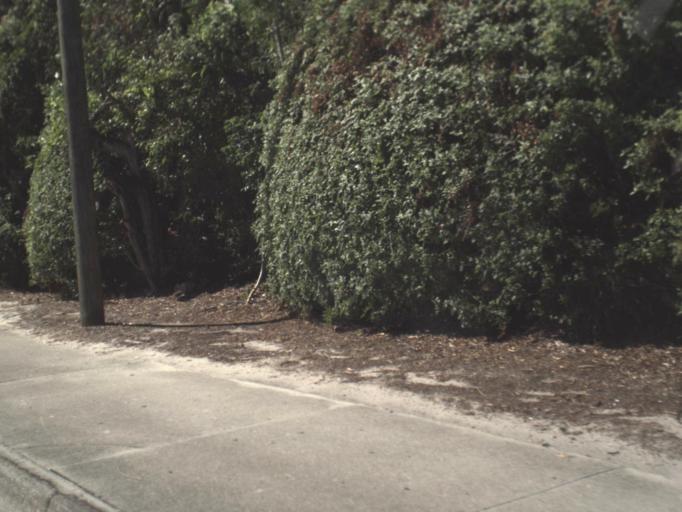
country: US
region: Florida
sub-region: Collier County
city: Pine Ridge
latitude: 26.2024
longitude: -81.7684
